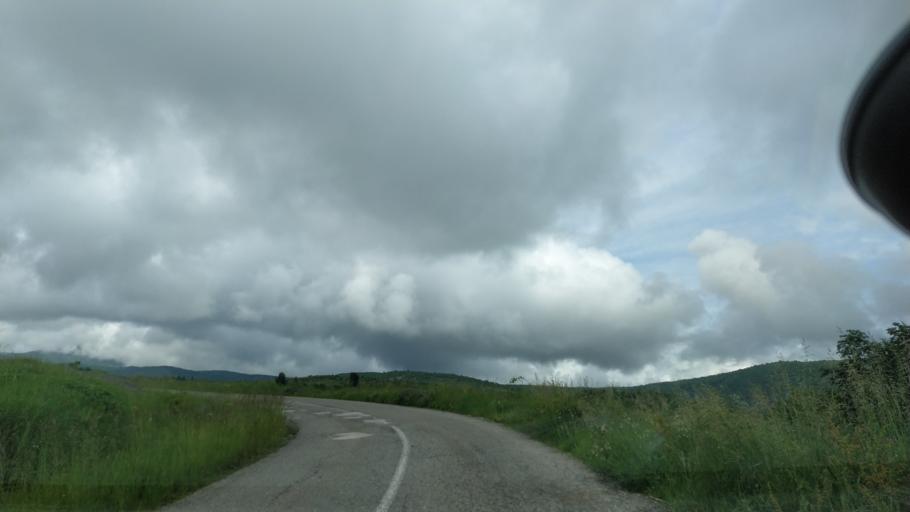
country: RS
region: Central Serbia
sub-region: Zajecarski Okrug
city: Soko Banja
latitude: 43.6982
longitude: 21.9391
